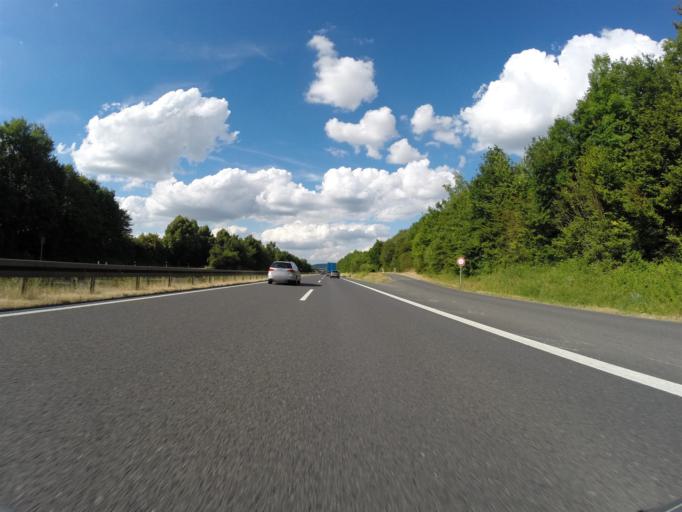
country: DE
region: Bavaria
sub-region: Upper Franconia
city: Bad Staffelstein
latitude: 50.1020
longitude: 11.0098
